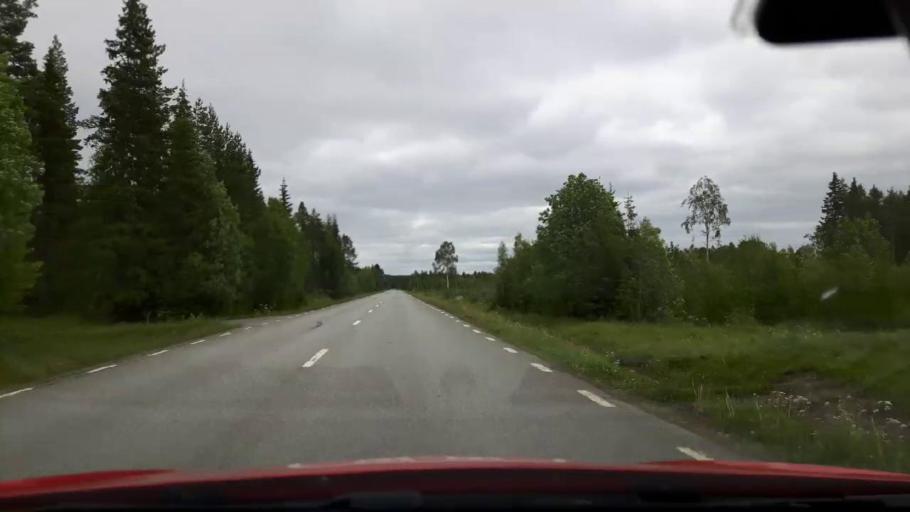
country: SE
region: Jaemtland
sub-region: Stroemsunds Kommun
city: Stroemsund
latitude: 63.5435
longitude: 15.4220
